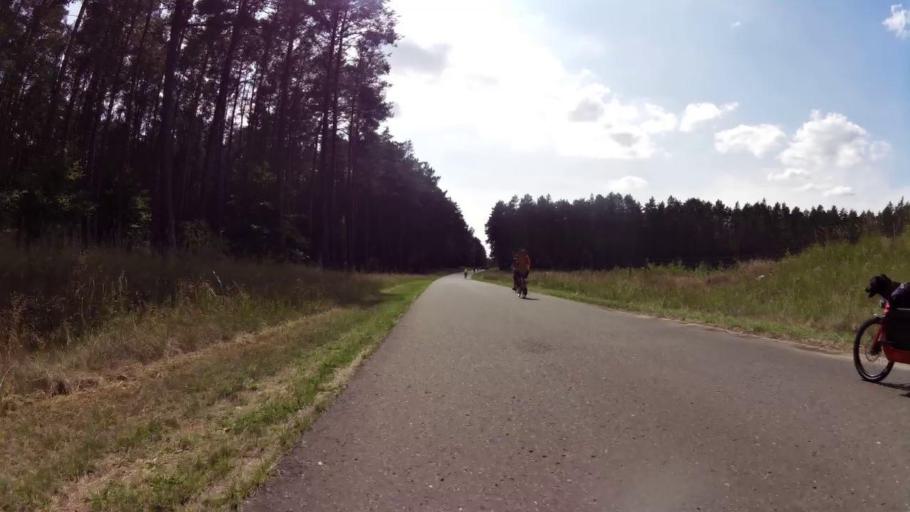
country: PL
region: West Pomeranian Voivodeship
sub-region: Powiat choszczenski
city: Drawno
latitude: 53.3669
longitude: 15.7180
